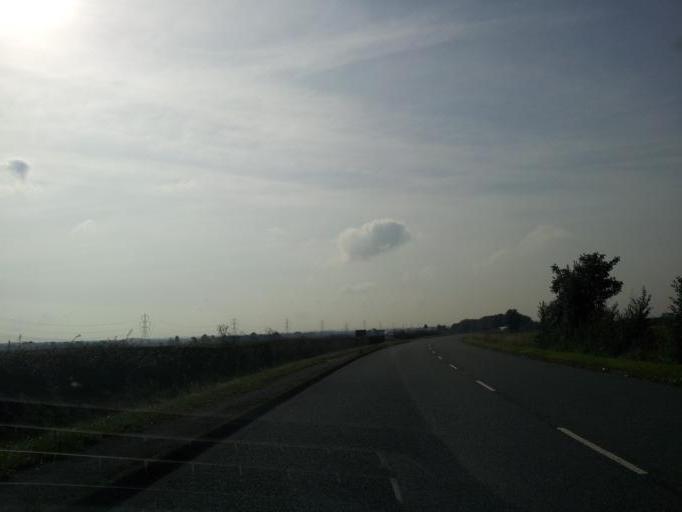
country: GB
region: England
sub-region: Lincolnshire
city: Long Bennington
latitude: 53.0341
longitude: -0.7690
